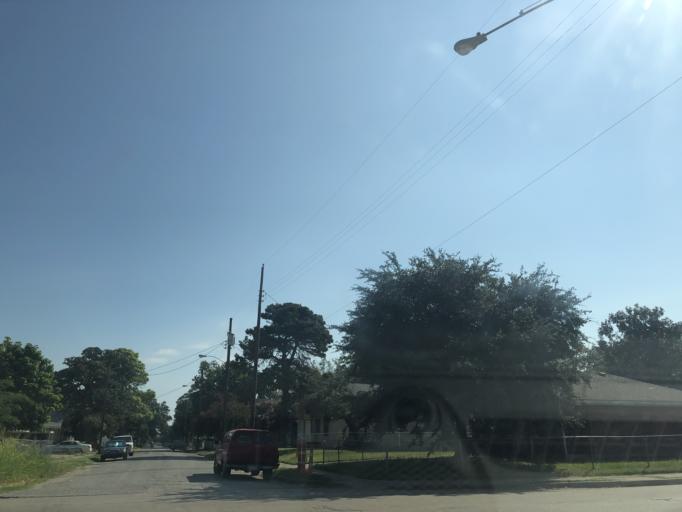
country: US
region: Texas
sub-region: Dallas County
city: Dallas
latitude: 32.7639
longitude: -96.7697
